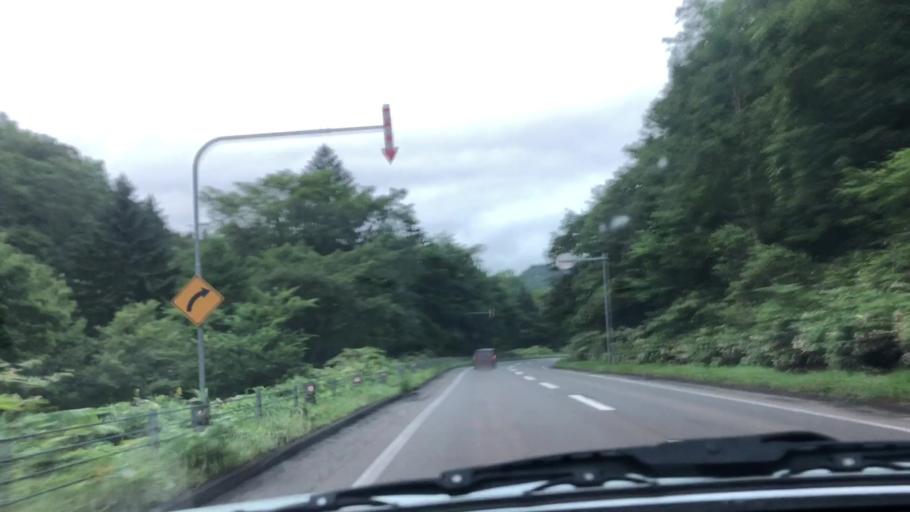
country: JP
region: Hokkaido
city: Iwamizawa
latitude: 42.8978
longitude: 142.1259
